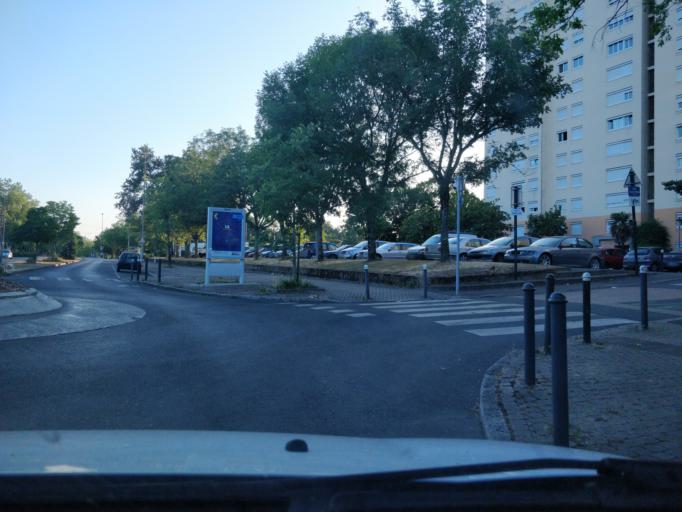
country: FR
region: Pays de la Loire
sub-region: Departement de la Loire-Atlantique
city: La Chapelle-sur-Erdre
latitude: 47.2604
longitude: -1.5747
